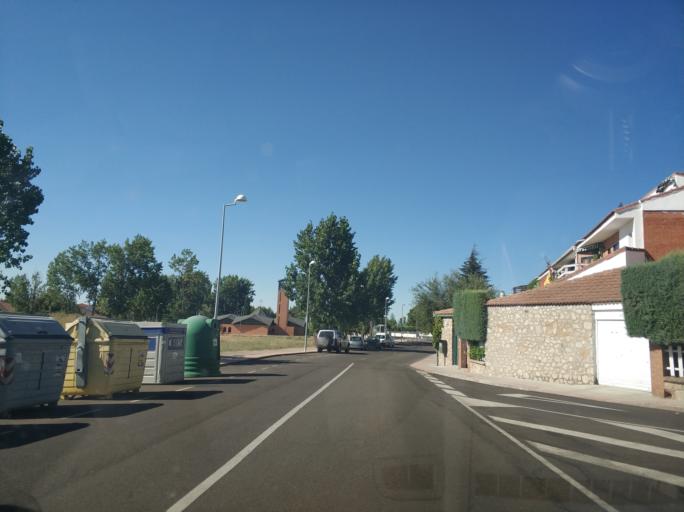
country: ES
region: Castille and Leon
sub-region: Provincia de Salamanca
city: Santa Marta de Tormes
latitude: 40.9361
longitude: -5.6253
